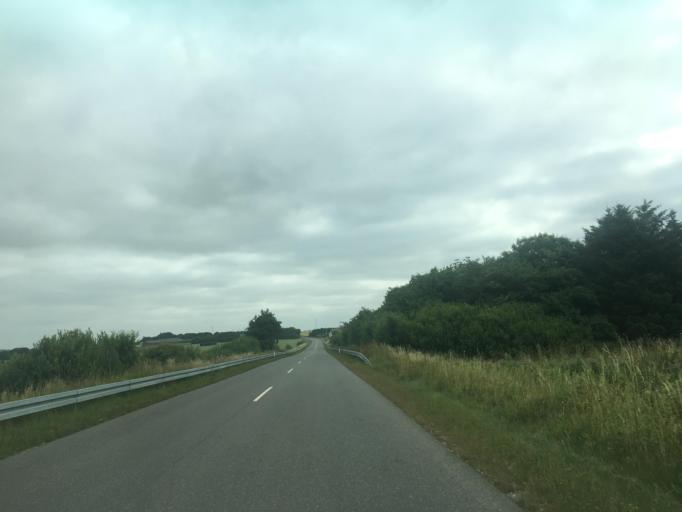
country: DK
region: North Denmark
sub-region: Thisted Kommune
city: Hurup
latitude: 56.8189
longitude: 8.5285
